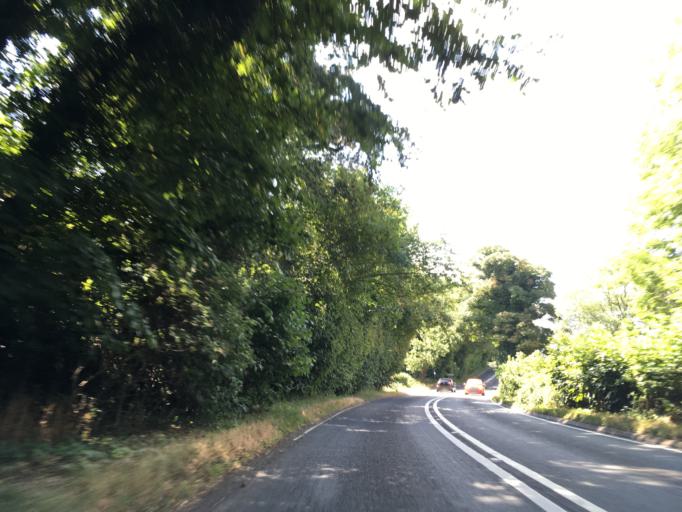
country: GB
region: England
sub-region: Gloucestershire
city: Churchdown
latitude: 51.8301
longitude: -2.1662
